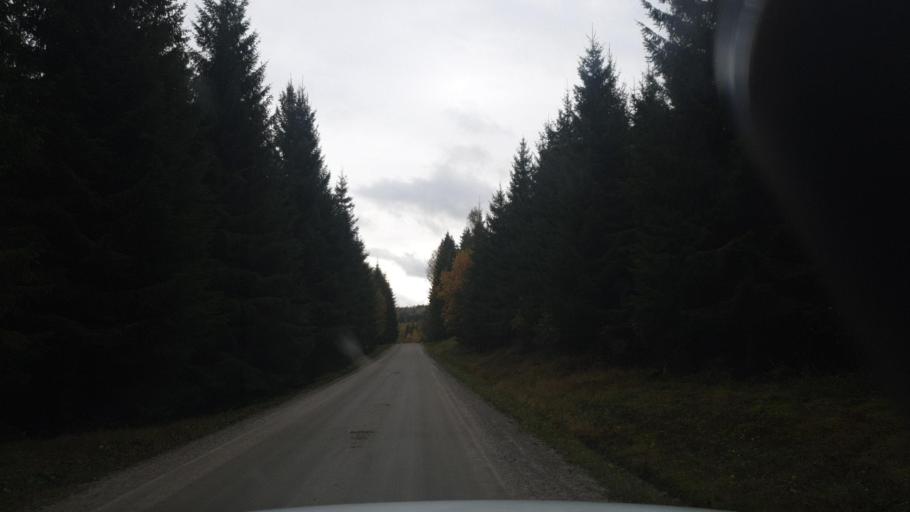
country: SE
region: Vaermland
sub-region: Arvika Kommun
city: Arvika
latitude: 59.7986
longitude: 12.7500
